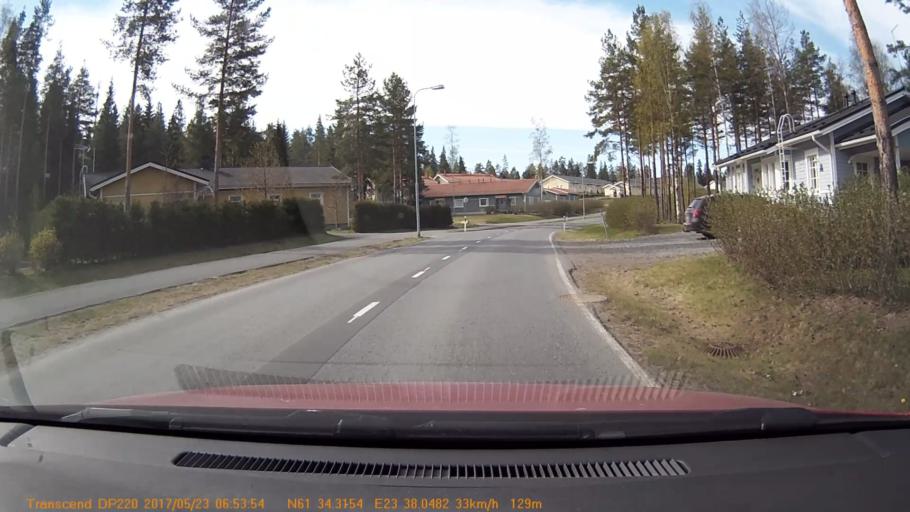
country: FI
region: Pirkanmaa
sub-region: Tampere
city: Yloejaervi
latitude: 61.5719
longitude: 23.6339
